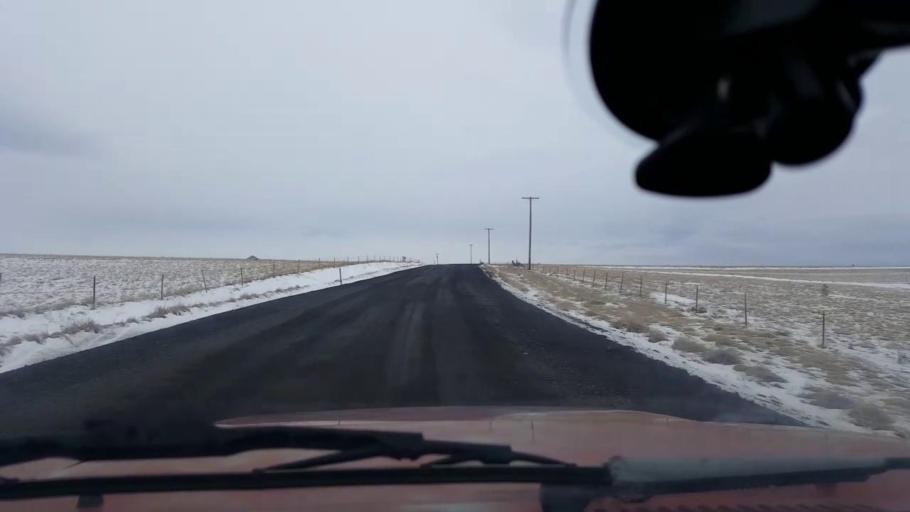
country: US
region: Washington
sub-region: Garfield County
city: Pomeroy
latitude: 46.3196
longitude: -117.4055
